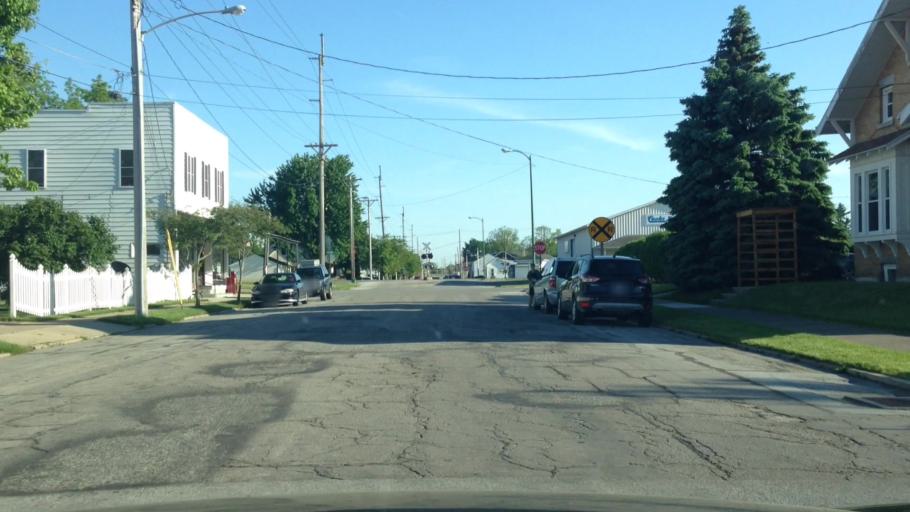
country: US
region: Ohio
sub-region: Auglaize County
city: Wapakoneta
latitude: 40.5695
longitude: -84.1928
